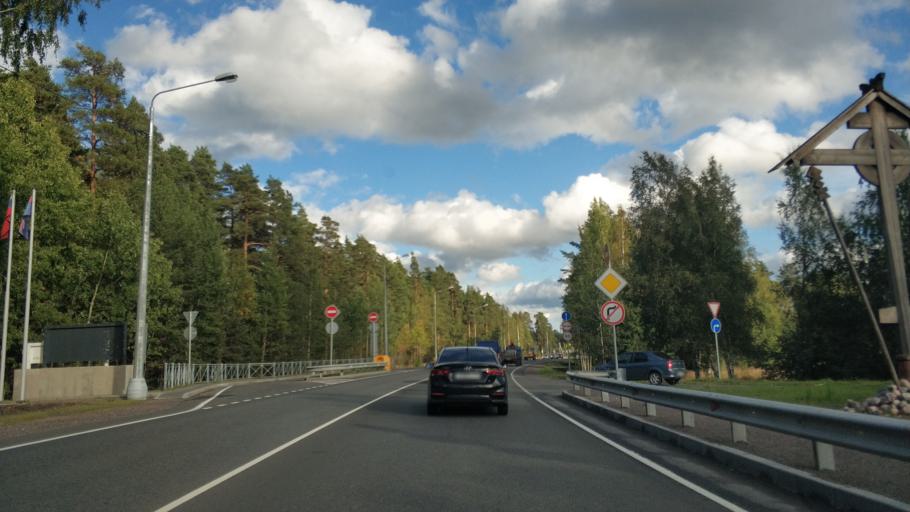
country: RU
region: Leningrad
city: Priozersk
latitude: 61.0090
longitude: 30.1705
